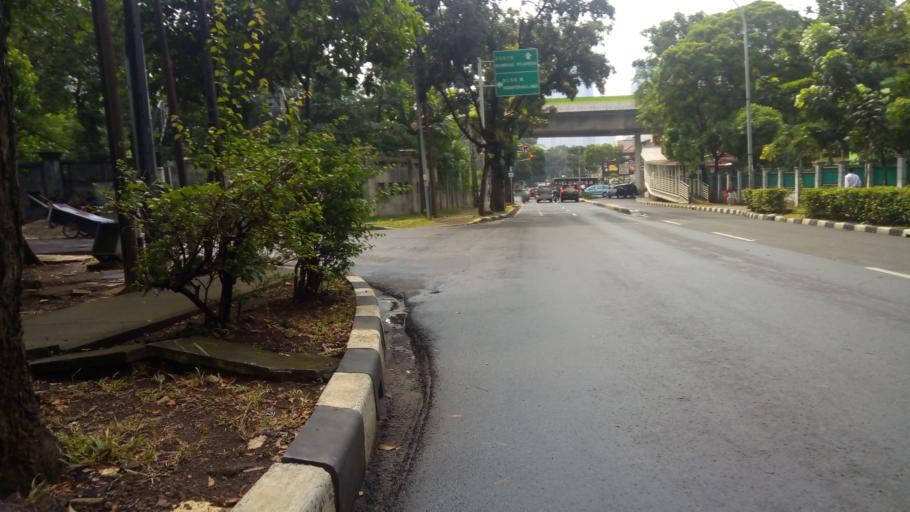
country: ID
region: Jakarta Raya
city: Jakarta
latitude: -6.2401
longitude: 106.8073
